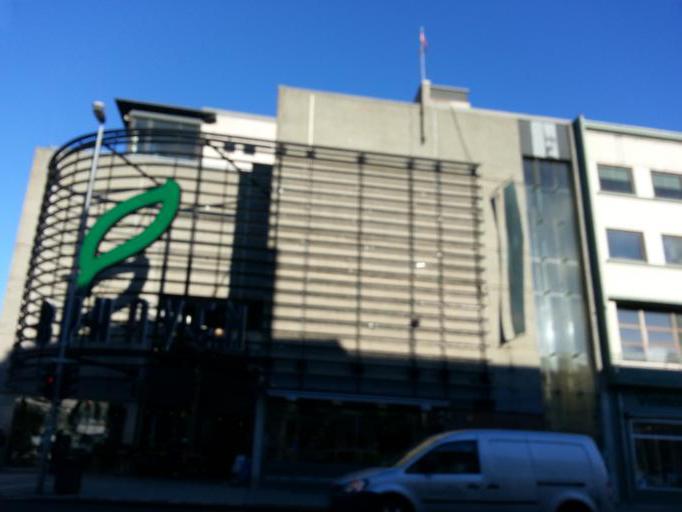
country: NO
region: Sor-Trondelag
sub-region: Trondheim
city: Trondheim
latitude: 63.4332
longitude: 10.3962
